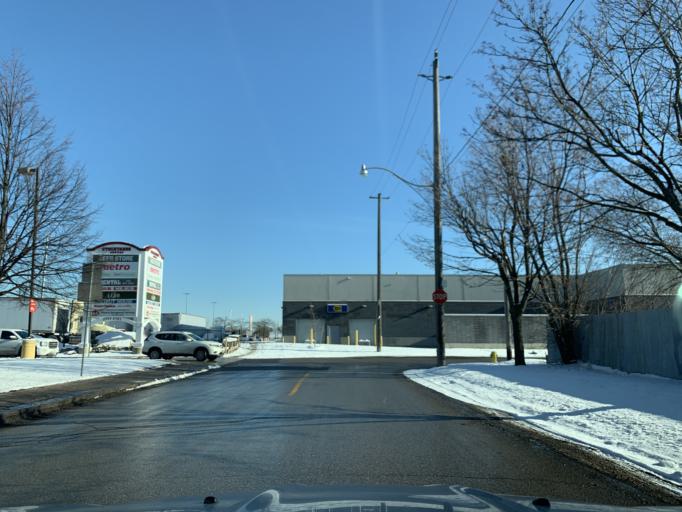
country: CA
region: Ontario
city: Toronto
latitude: 43.6692
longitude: -79.4725
